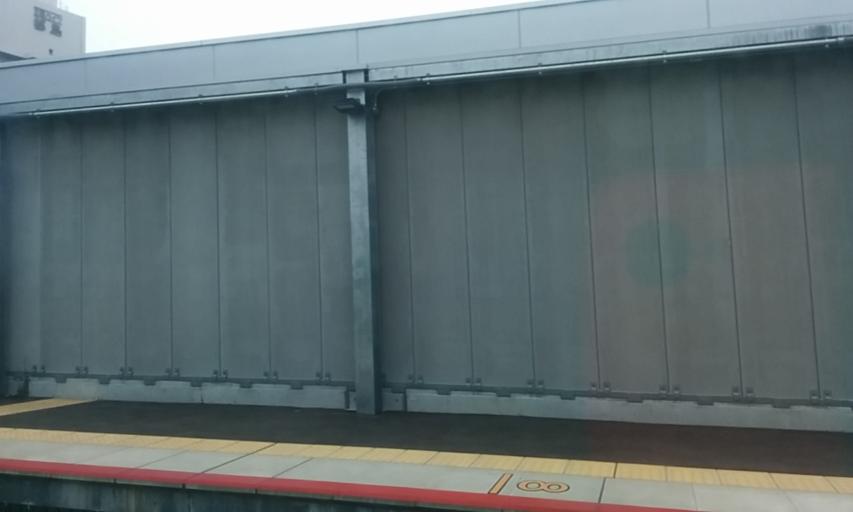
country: JP
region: Osaka
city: Moriguchi
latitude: 34.7232
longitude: 135.5308
